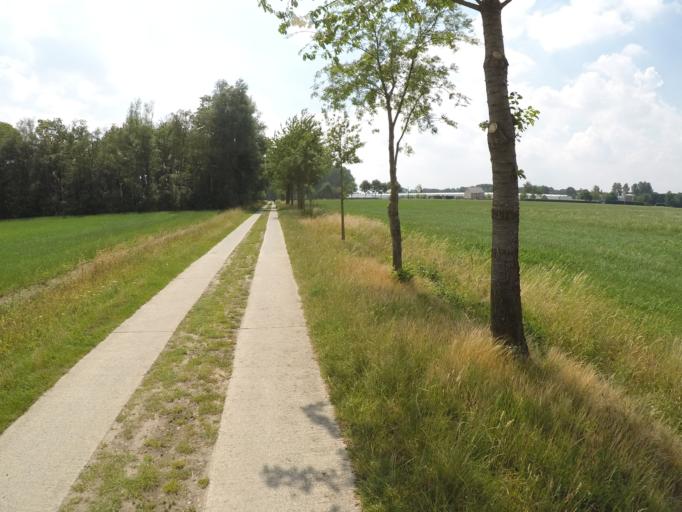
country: BE
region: Flanders
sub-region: Provincie Antwerpen
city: Rijkevorsel
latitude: 51.3432
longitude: 4.7347
